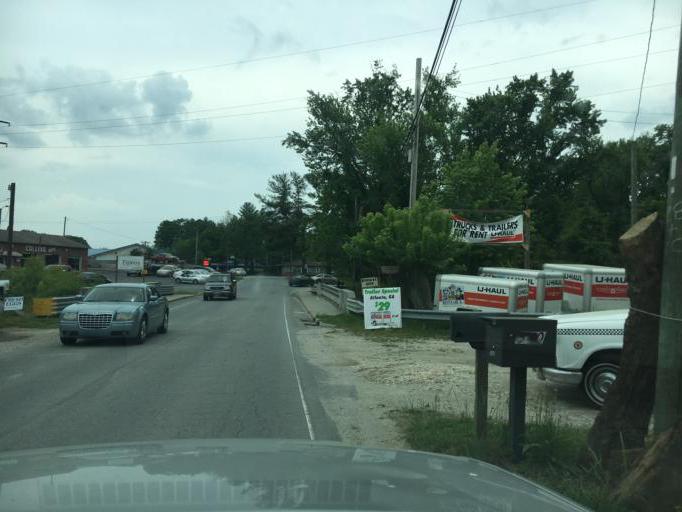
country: US
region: North Carolina
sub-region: Henderson County
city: Hendersonville
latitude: 35.3111
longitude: -82.4552
